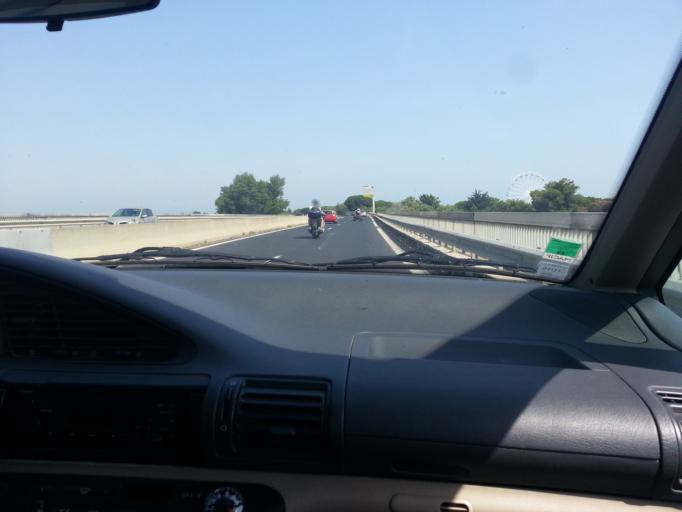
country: FR
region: Languedoc-Roussillon
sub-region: Departement de l'Herault
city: Perols
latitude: 43.5505
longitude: 3.9787
